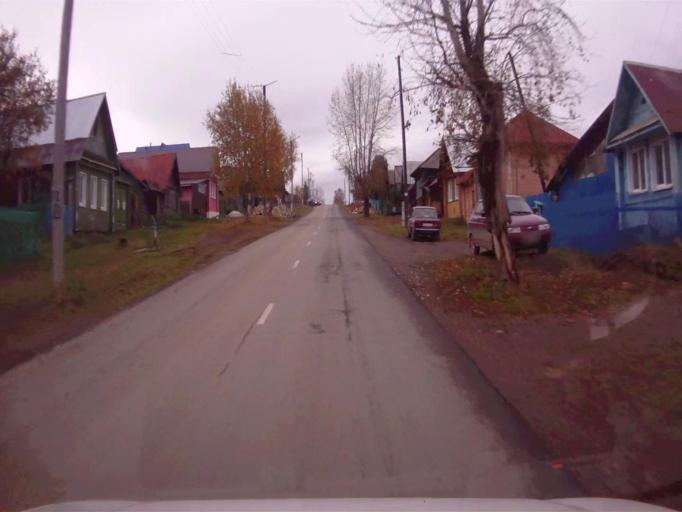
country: RU
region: Chelyabinsk
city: Nyazepetrovsk
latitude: 56.0597
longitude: 59.5812
